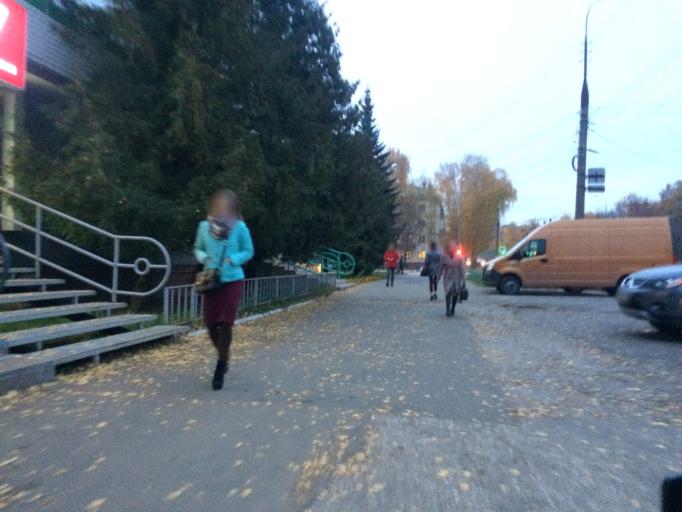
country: RU
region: Mariy-El
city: Yoshkar-Ola
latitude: 56.6229
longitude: 47.8850
